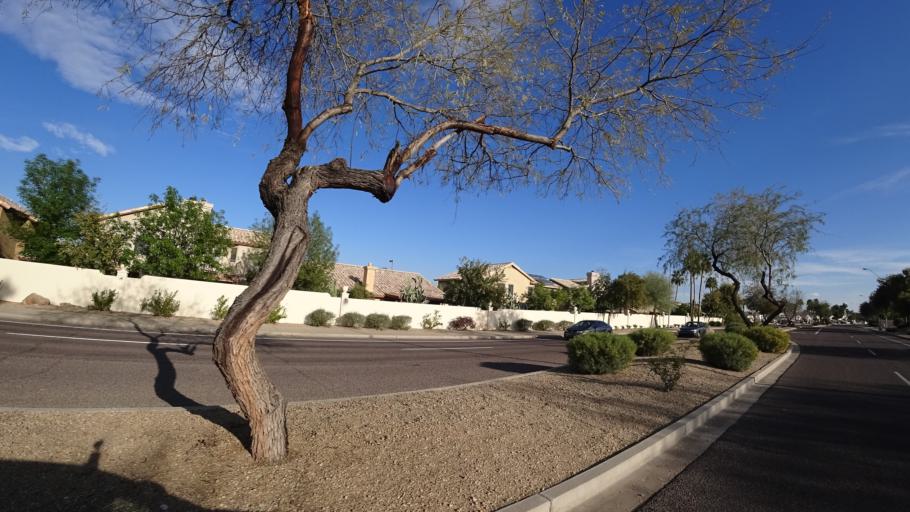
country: US
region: Arizona
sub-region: Maricopa County
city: Sun City
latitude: 33.6186
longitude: -112.2546
